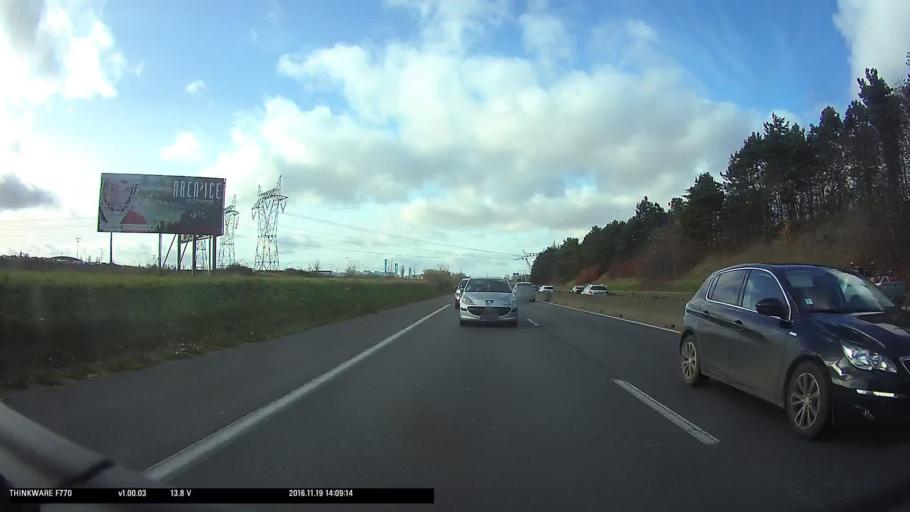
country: FR
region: Ile-de-France
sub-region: Departement du Val-d'Oise
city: Osny
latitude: 49.0551
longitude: 2.0541
